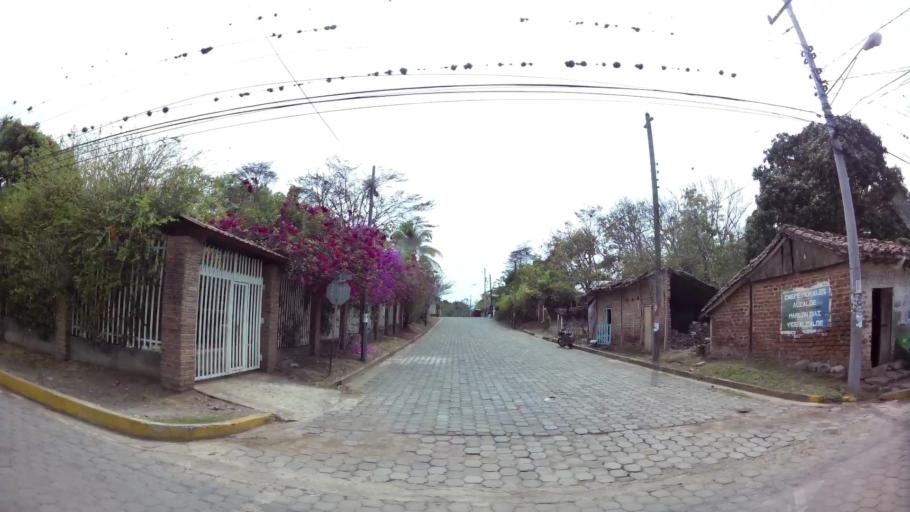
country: NI
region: Granada
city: Diriomo
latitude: 11.8782
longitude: -86.0526
